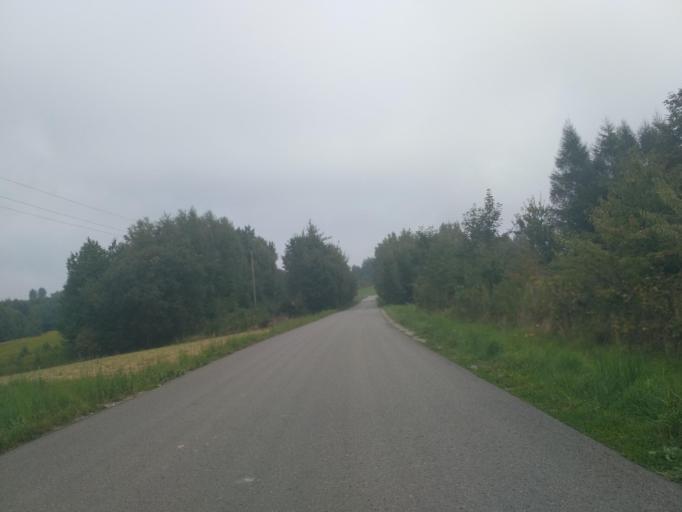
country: PL
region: Subcarpathian Voivodeship
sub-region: Powiat rzeszowski
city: Chmielnik
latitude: 50.0065
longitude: 22.1232
